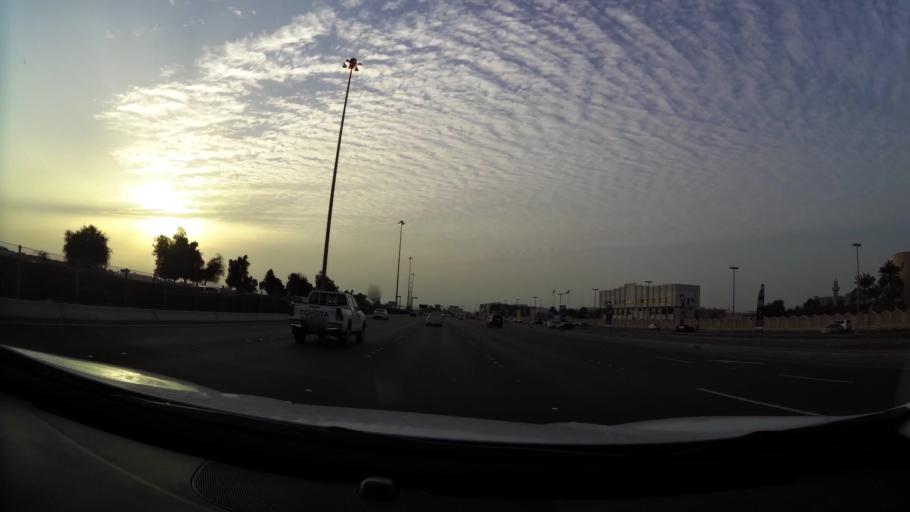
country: AE
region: Abu Dhabi
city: Abu Dhabi
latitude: 24.4184
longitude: 54.4319
